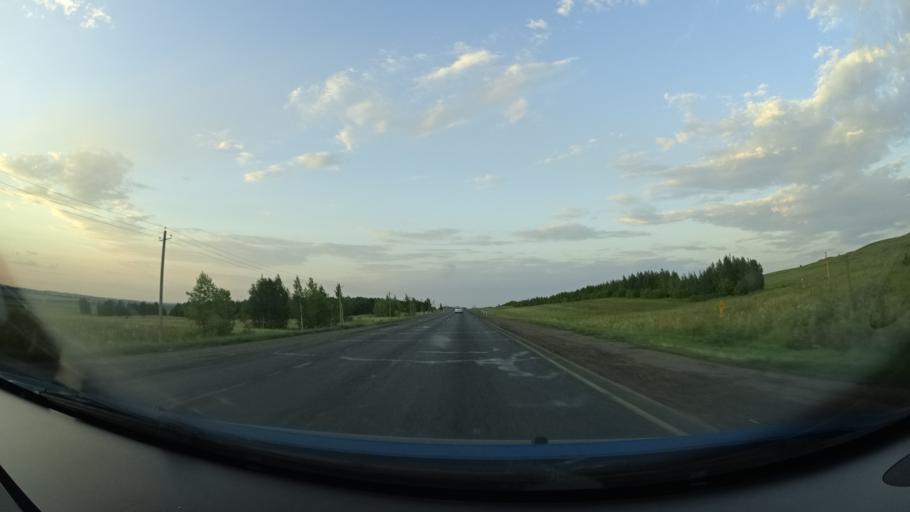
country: RU
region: Orenburg
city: Severnoye
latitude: 54.1973
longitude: 52.6840
